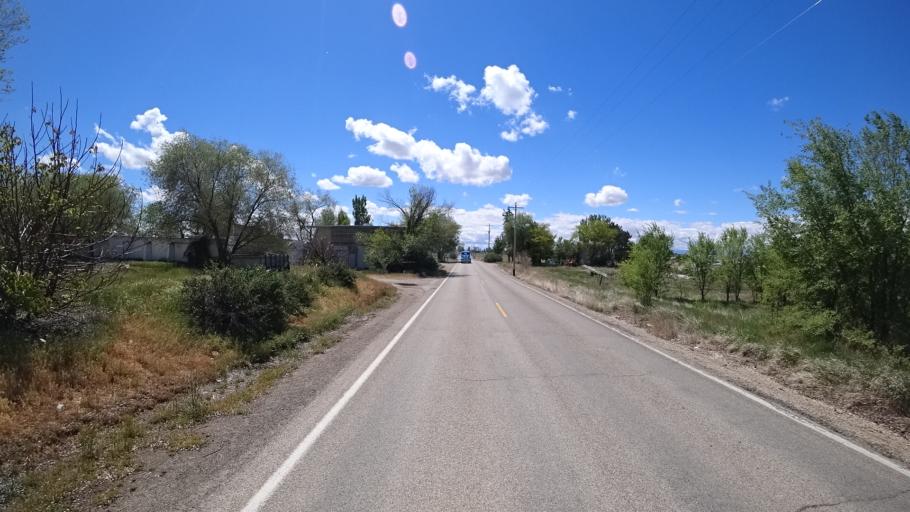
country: US
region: Idaho
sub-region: Ada County
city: Kuna
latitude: 43.4719
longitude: -116.3545
